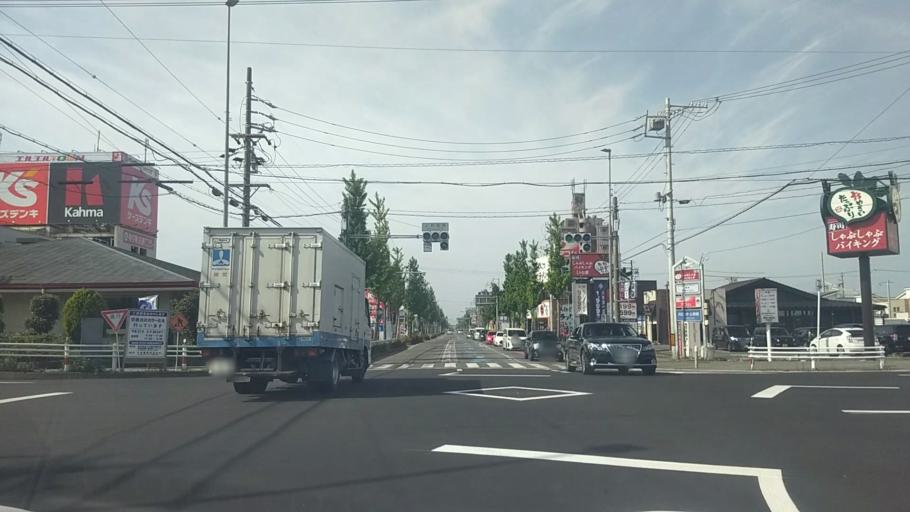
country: JP
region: Aichi
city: Okazaki
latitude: 34.9345
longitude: 137.1457
